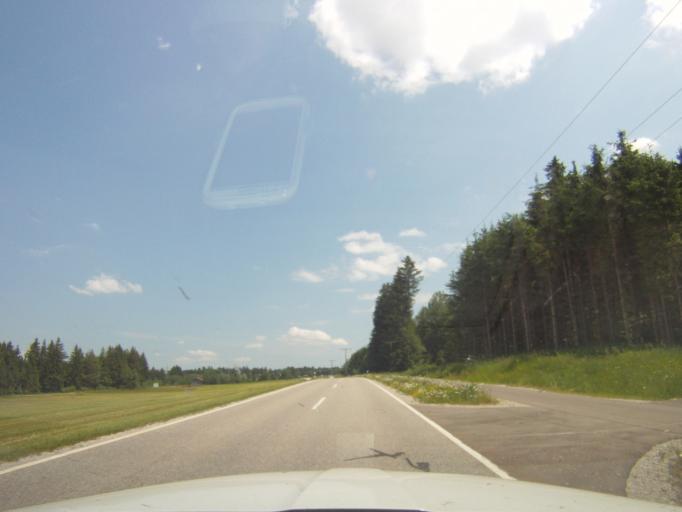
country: DE
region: Bavaria
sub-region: Swabia
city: Oy-Mittelberg
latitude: 47.6141
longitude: 10.4632
